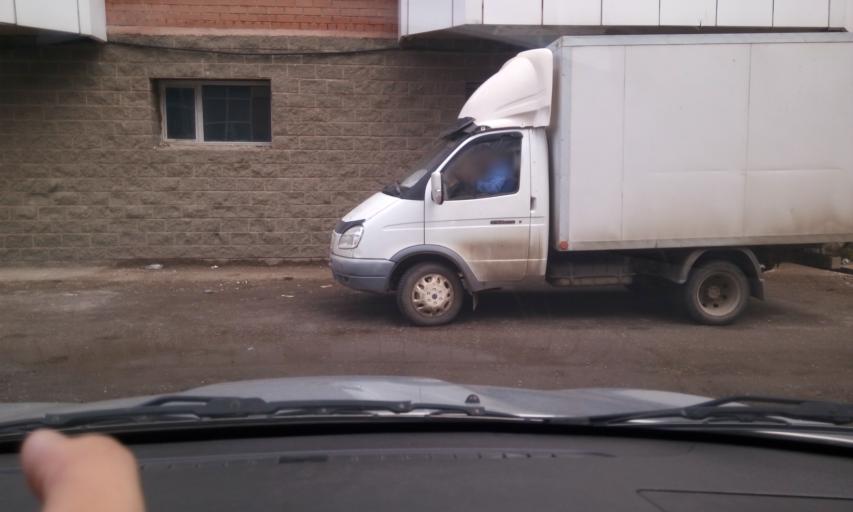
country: KZ
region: Astana Qalasy
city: Astana
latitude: 51.1679
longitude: 71.4013
